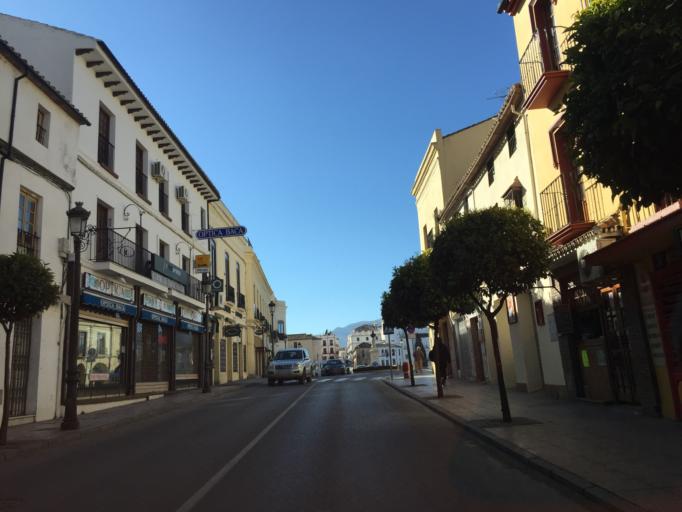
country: ES
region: Andalusia
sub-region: Provincia de Malaga
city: Ronda
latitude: 36.7419
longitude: -5.1664
